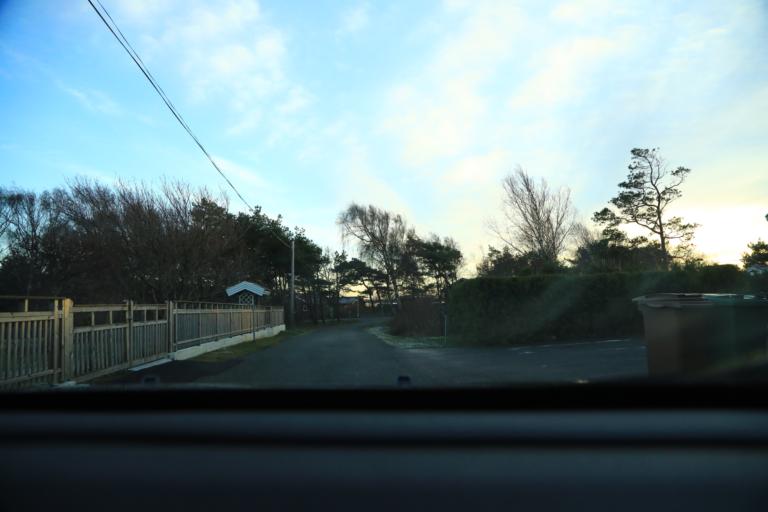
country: SE
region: Halland
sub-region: Varbergs Kommun
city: Varberg
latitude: 57.1878
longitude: 12.1662
